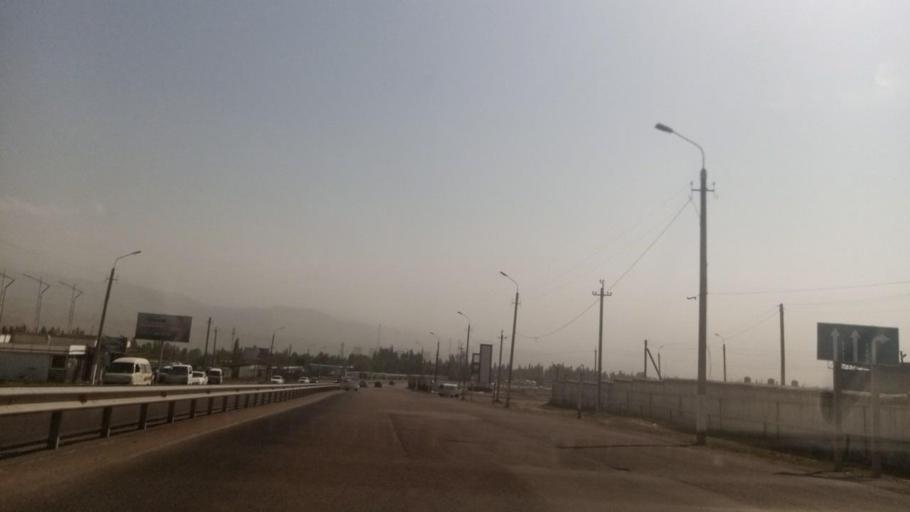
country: UZ
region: Toshkent
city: Angren
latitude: 41.0292
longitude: 70.1372
